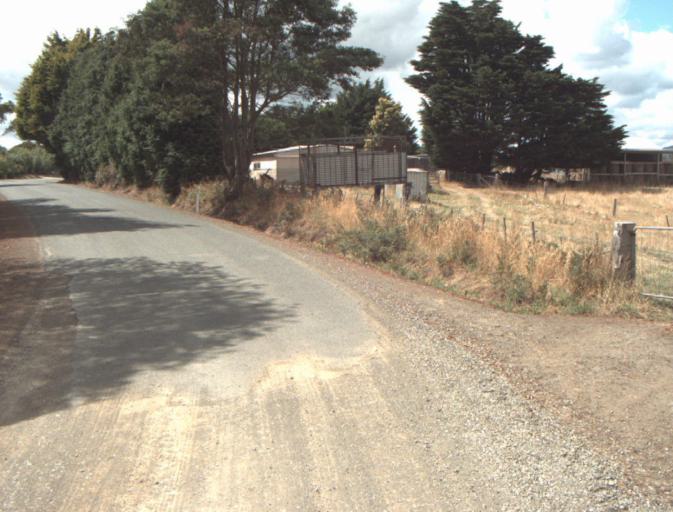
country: AU
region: Tasmania
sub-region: Launceston
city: Mayfield
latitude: -41.1934
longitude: 147.1911
